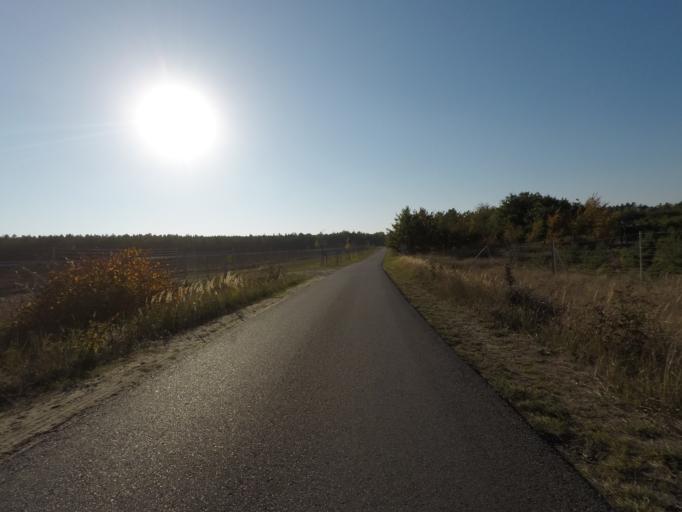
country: DE
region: Brandenburg
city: Marienwerder
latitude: 52.8310
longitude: 13.6653
